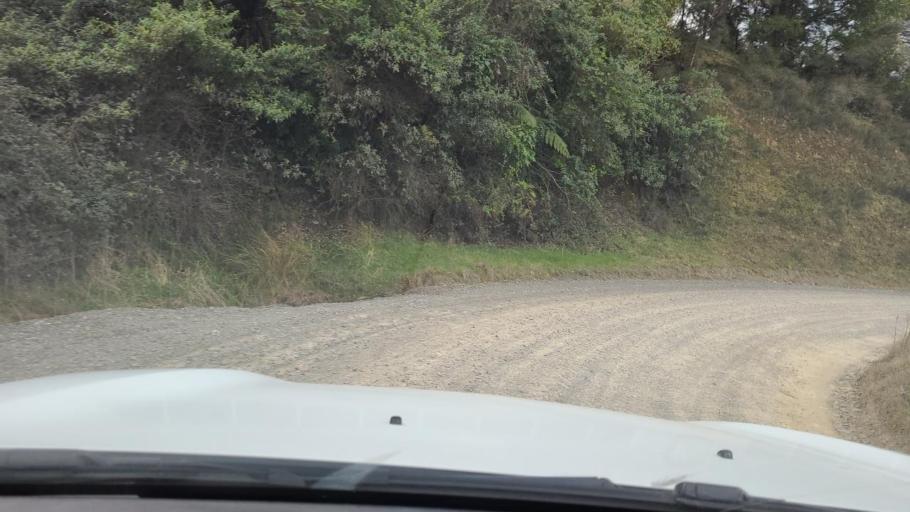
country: NZ
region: Hawke's Bay
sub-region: Napier City
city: Napier
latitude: -39.3029
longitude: 176.8275
